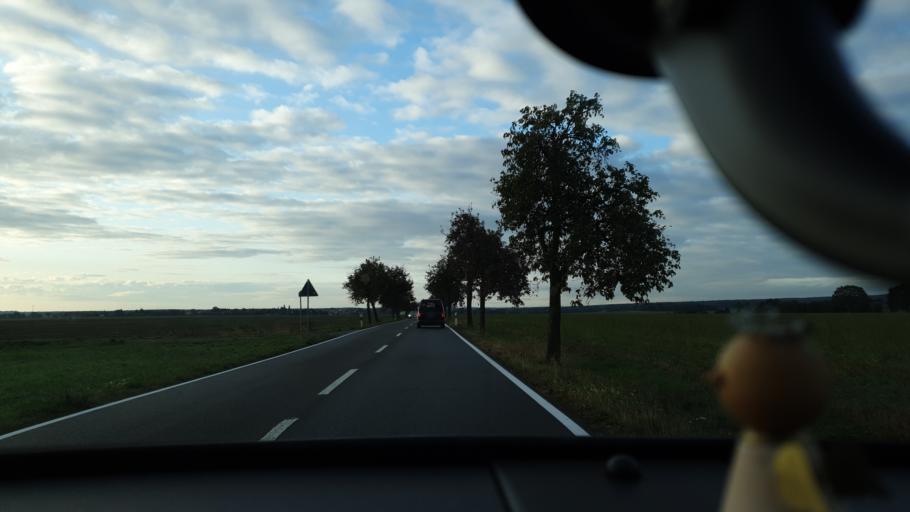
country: DE
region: Saxony
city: Schildau
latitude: 51.4749
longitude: 12.9248
